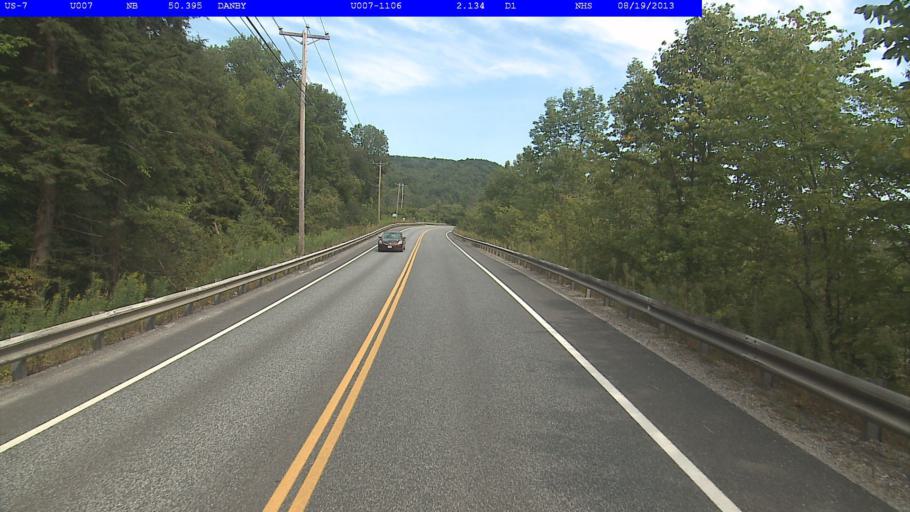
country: US
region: Vermont
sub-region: Rutland County
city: West Rutland
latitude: 43.3927
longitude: -72.9979
